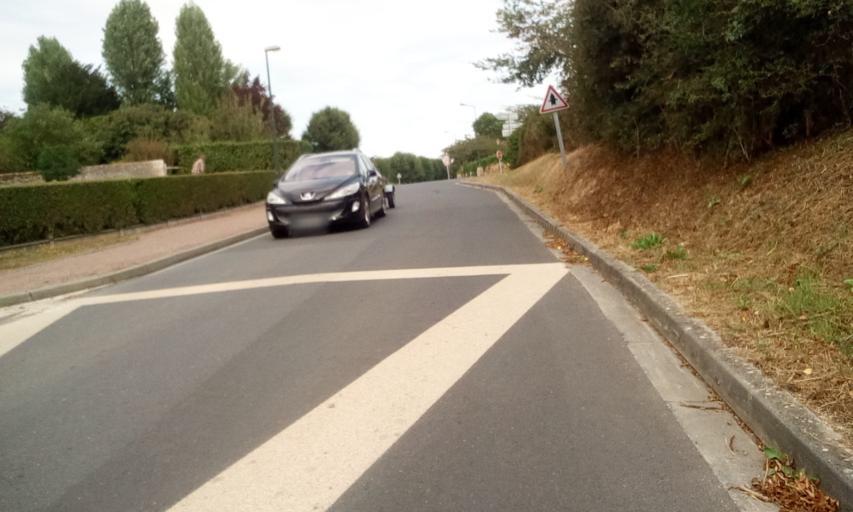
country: FR
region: Lower Normandy
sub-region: Departement du Calvados
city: Amfreville
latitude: 49.2397
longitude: -0.2267
